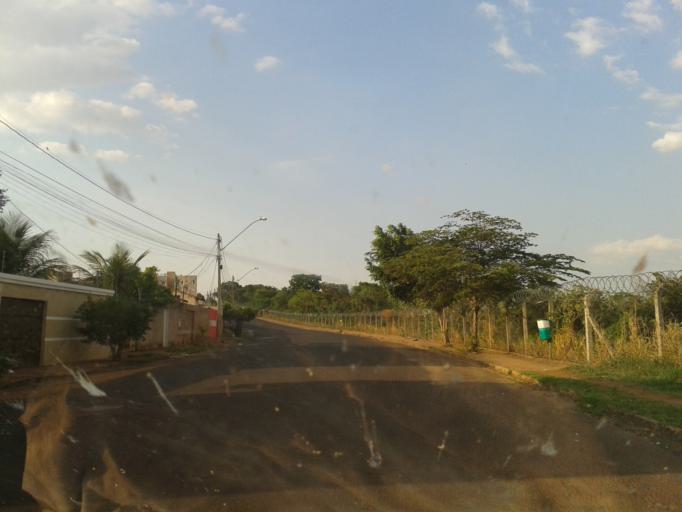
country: BR
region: Minas Gerais
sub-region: Uberlandia
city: Uberlandia
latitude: -18.9648
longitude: -48.3117
